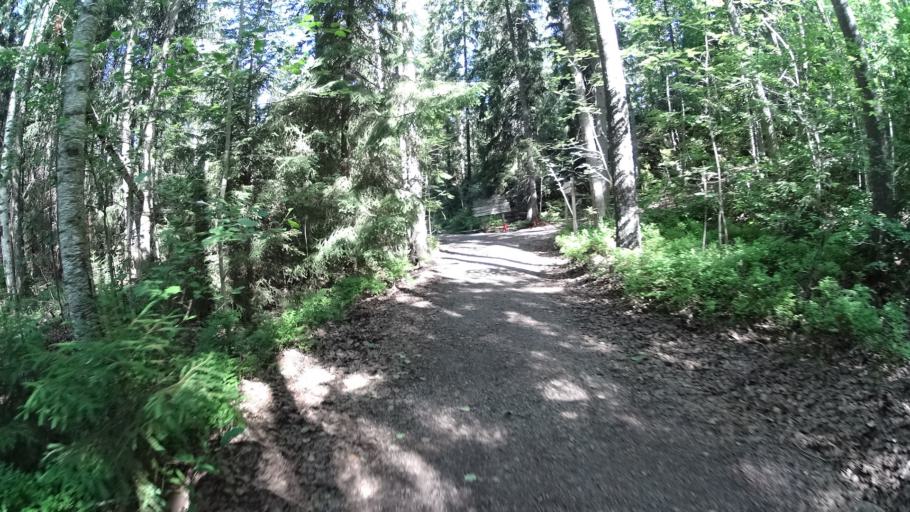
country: FI
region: Uusimaa
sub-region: Helsinki
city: Espoo
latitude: 60.3147
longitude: 24.5071
